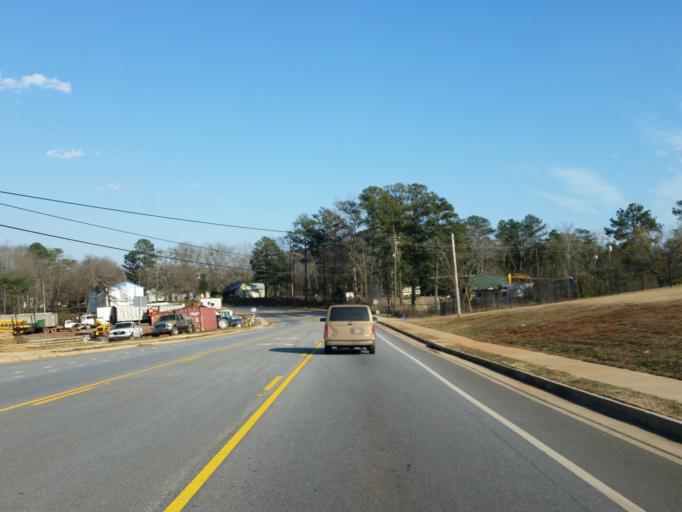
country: US
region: Georgia
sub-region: Monroe County
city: Forsyth
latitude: 33.0313
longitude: -83.9600
